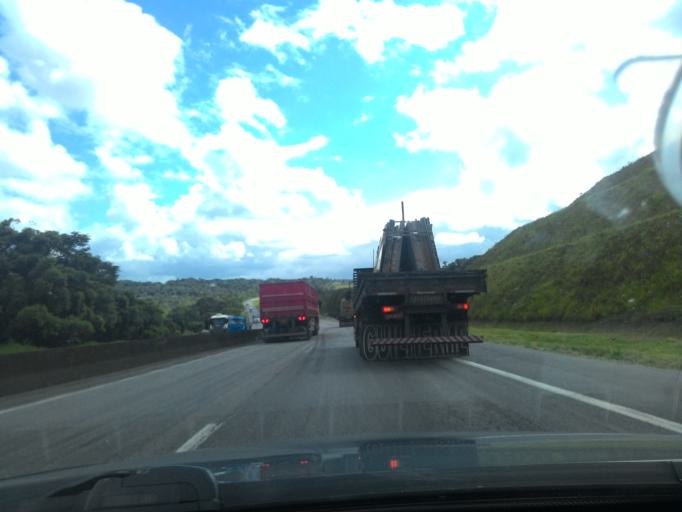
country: BR
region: Sao Paulo
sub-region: Cajati
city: Cajati
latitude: -24.9155
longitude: -48.2556
